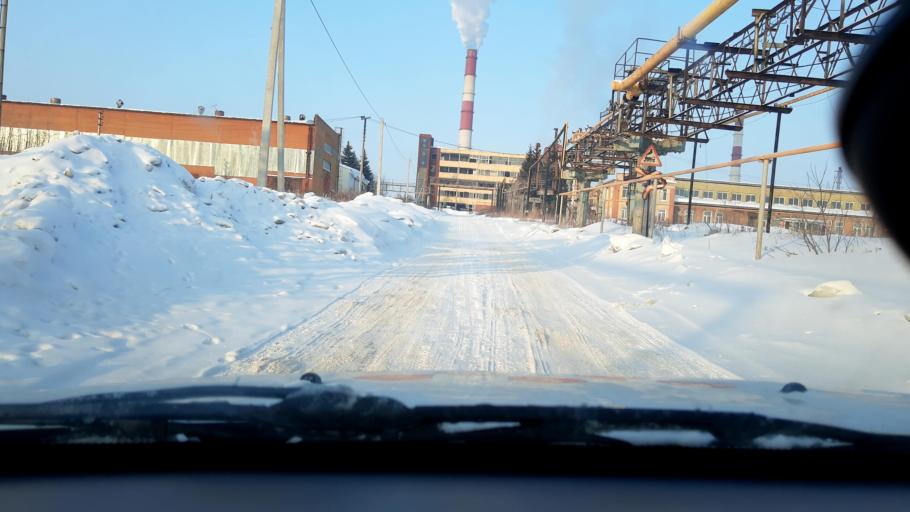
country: RU
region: Bashkortostan
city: Ufa
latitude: 54.8396
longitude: 56.1005
